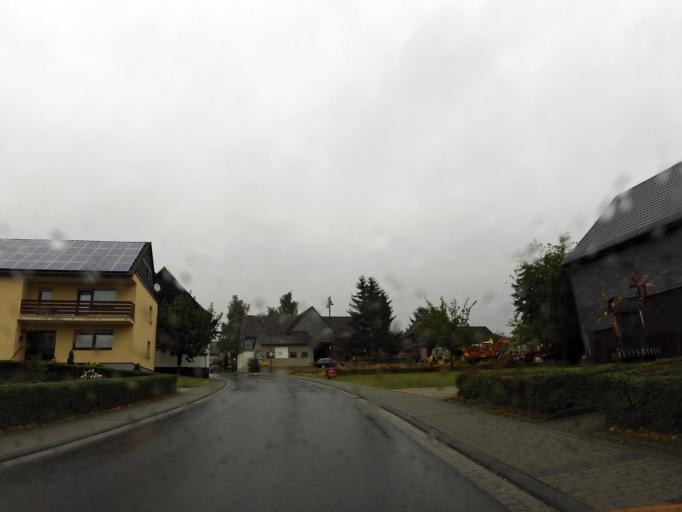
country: DE
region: Rheinland-Pfalz
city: Laubach
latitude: 50.0544
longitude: 7.5121
